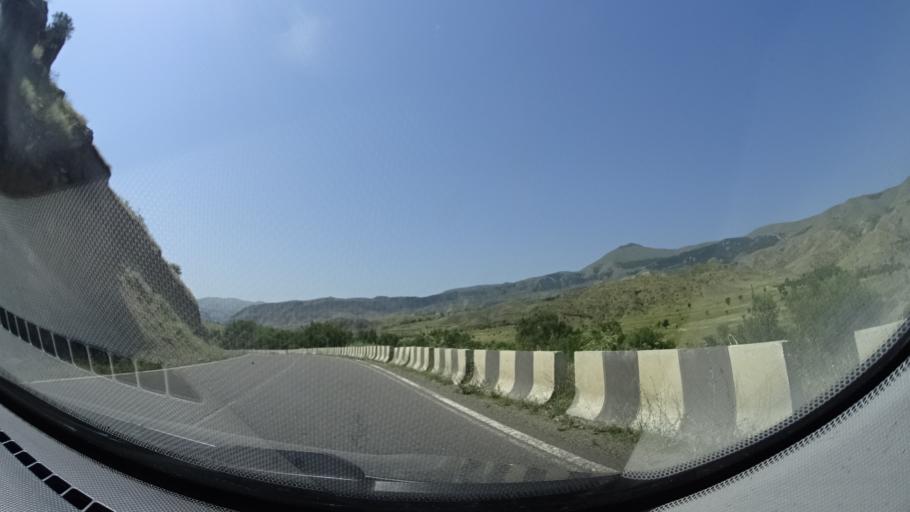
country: GE
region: Samtskhe-Javakheti
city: Aspindza
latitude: 41.5244
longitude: 43.2595
